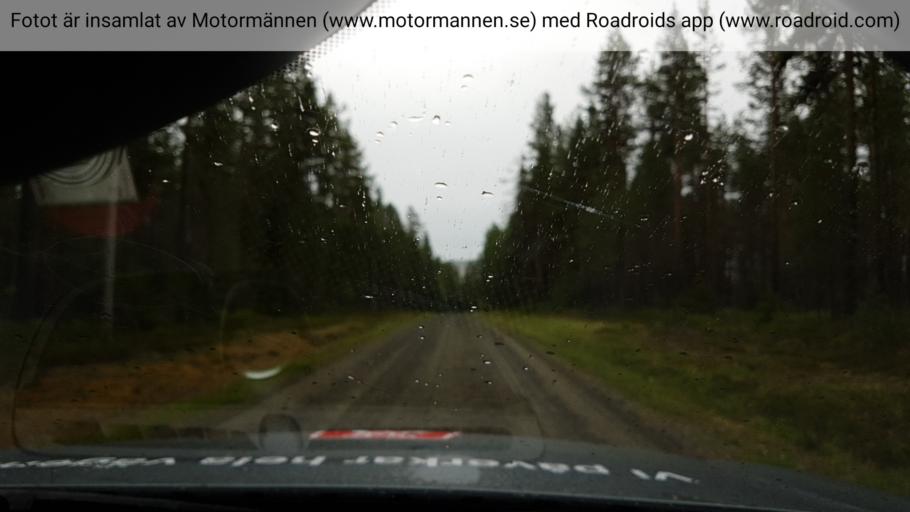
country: SE
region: Jaemtland
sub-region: Bergs Kommun
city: Hoverberg
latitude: 62.5005
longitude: 14.7053
